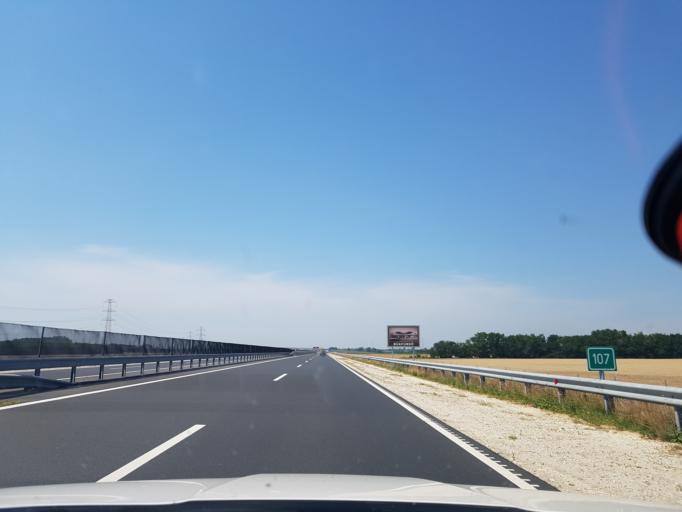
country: HU
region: Vas
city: Repcelak
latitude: 47.3673
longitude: 16.9253
